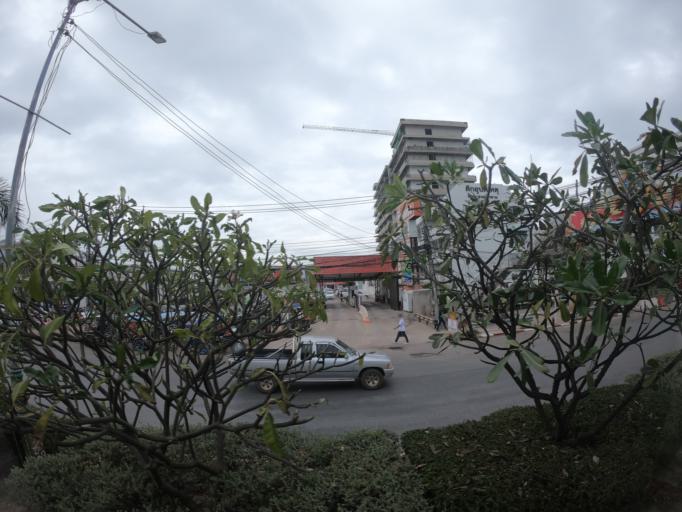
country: TH
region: Maha Sarakham
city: Maha Sarakham
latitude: 16.1804
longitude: 103.2992
